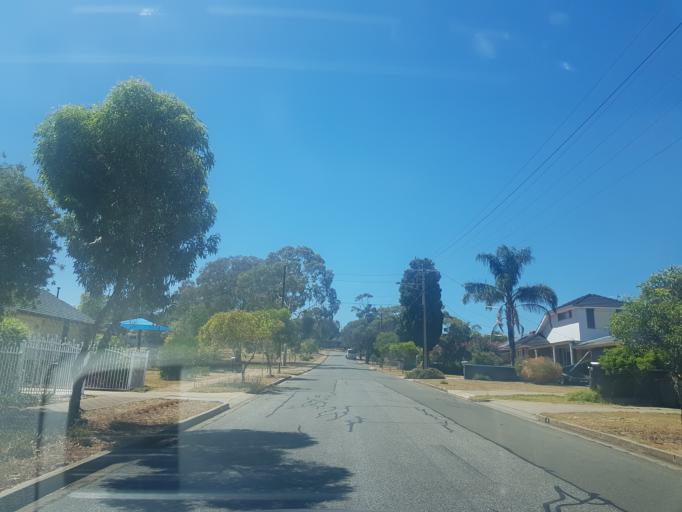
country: AU
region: South Australia
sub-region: Salisbury
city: Ingle Farm
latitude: -34.8174
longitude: 138.6490
